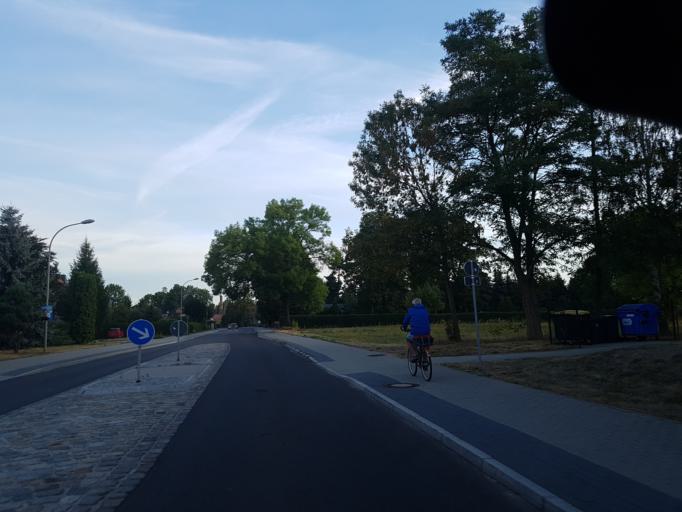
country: DE
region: Brandenburg
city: Sonnewalde
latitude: 51.6903
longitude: 13.6473
